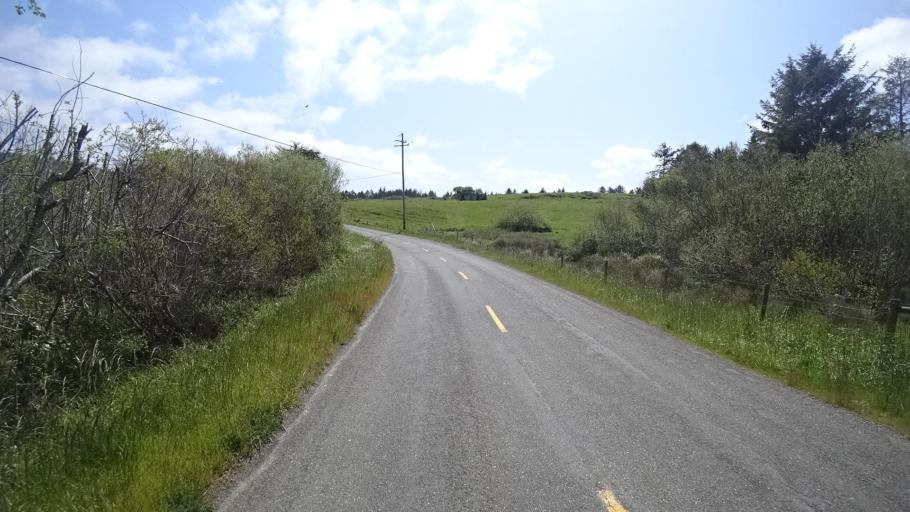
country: US
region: California
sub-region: Humboldt County
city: Humboldt Hill
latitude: 40.6693
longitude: -124.2083
